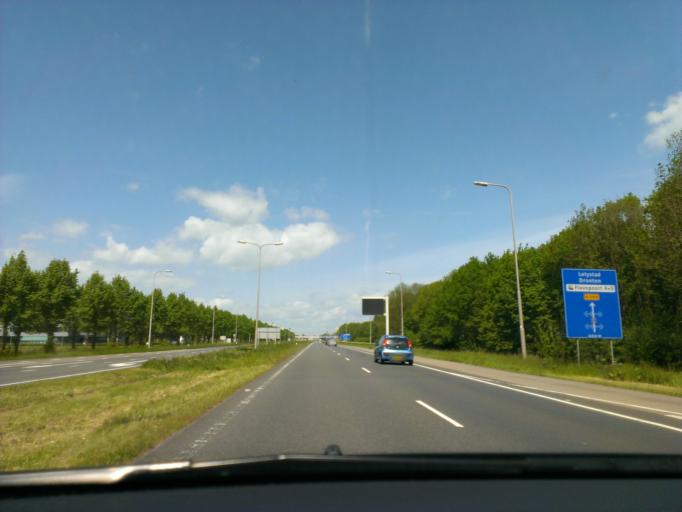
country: NL
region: Flevoland
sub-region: Gemeente Lelystad
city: Lelystad
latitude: 52.4746
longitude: 5.5119
